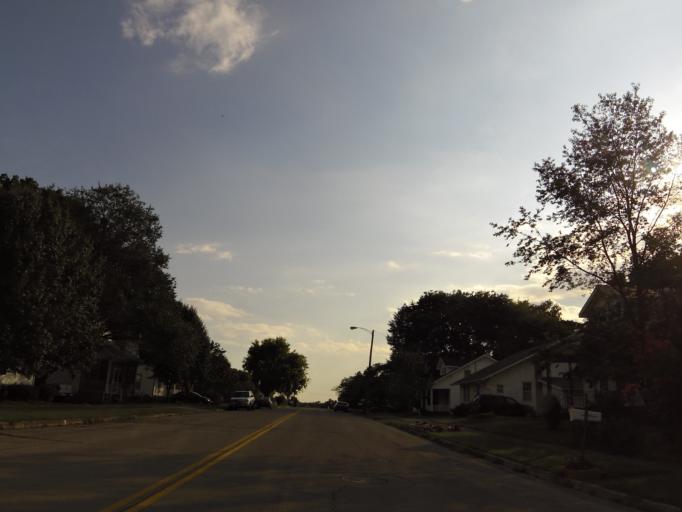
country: US
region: Tennessee
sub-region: Blount County
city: Maryville
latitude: 35.7643
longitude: -83.9772
